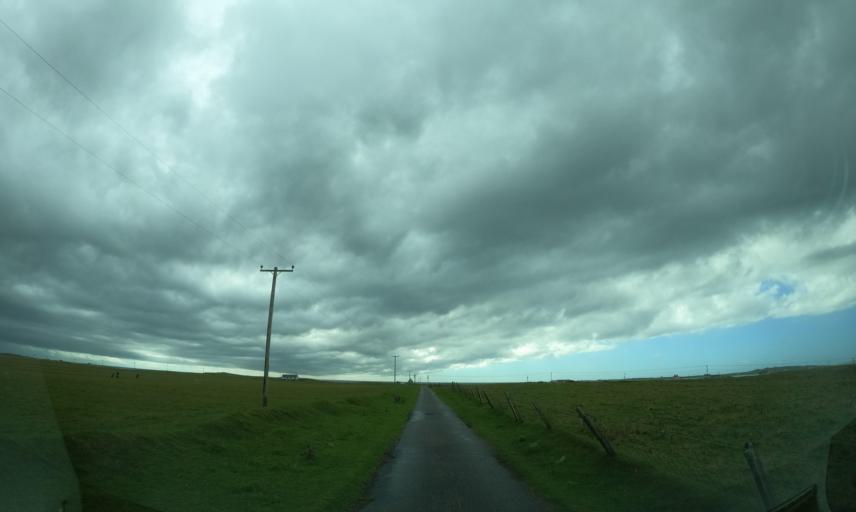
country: GB
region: Scotland
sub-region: Eilean Siar
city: Barra
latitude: 56.5314
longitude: -6.7975
